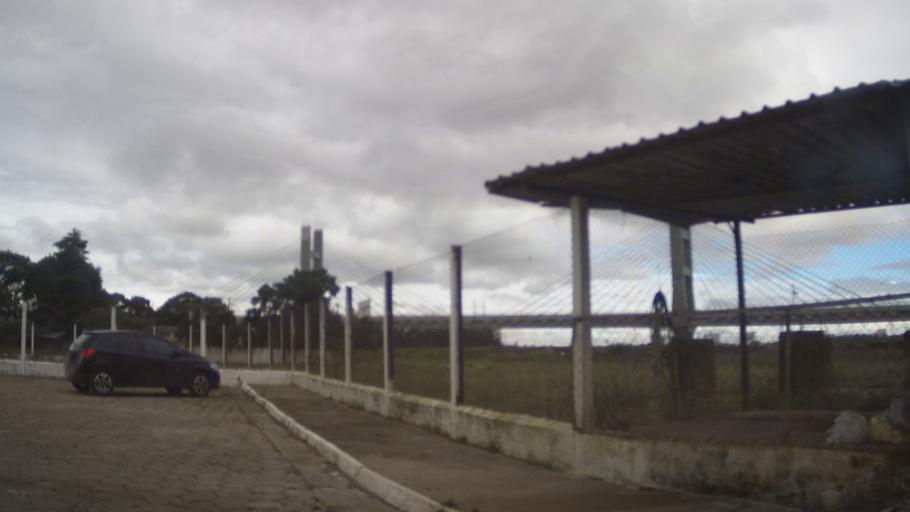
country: BR
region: Sao Paulo
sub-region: Guarulhos
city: Guarulhos
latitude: -23.4713
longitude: -46.4960
